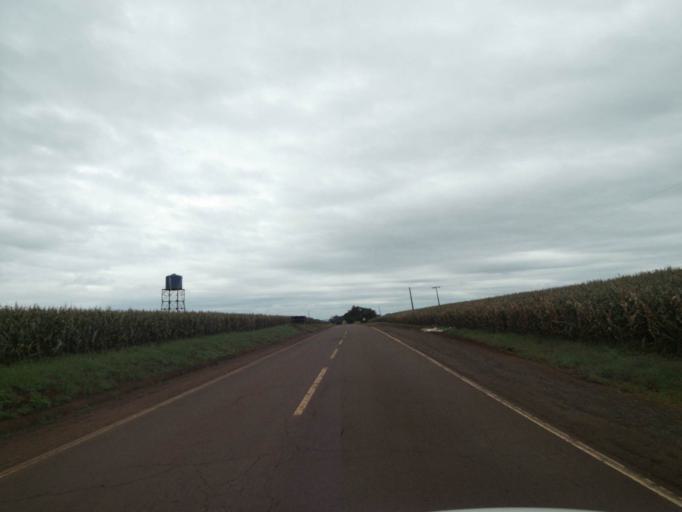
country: BR
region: Parana
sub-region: Marechal Candido Rondon
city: Marechal Candido Rondon
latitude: -24.8024
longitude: -54.2036
